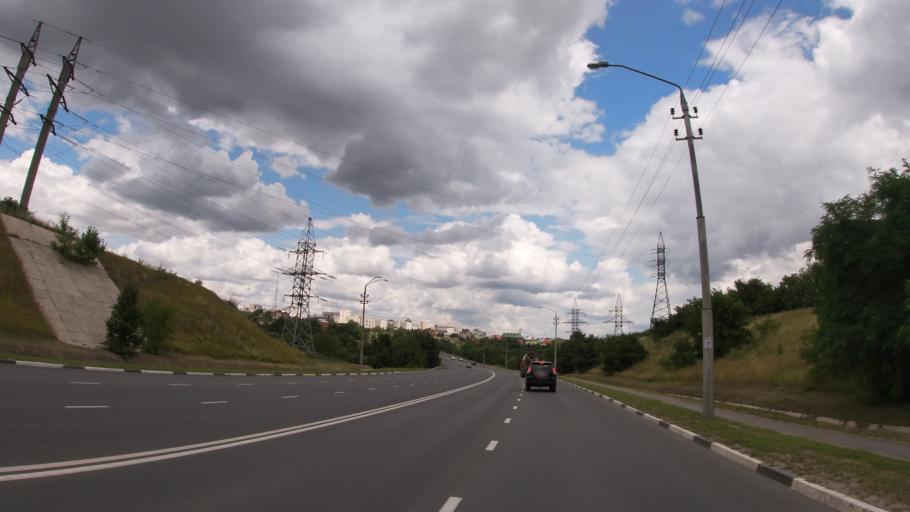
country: RU
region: Belgorod
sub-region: Belgorodskiy Rayon
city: Belgorod
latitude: 50.5571
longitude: 36.5855
